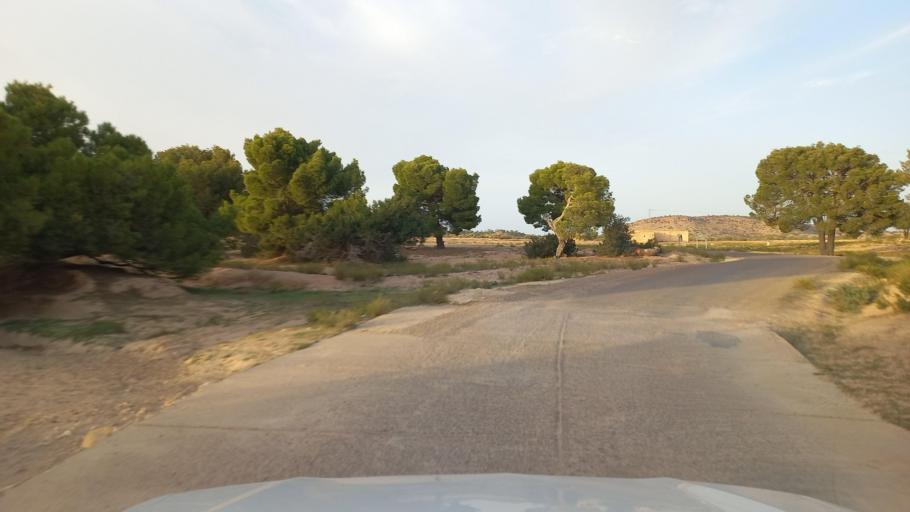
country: TN
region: Al Qasrayn
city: Sbiba
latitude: 35.4132
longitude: 8.9268
